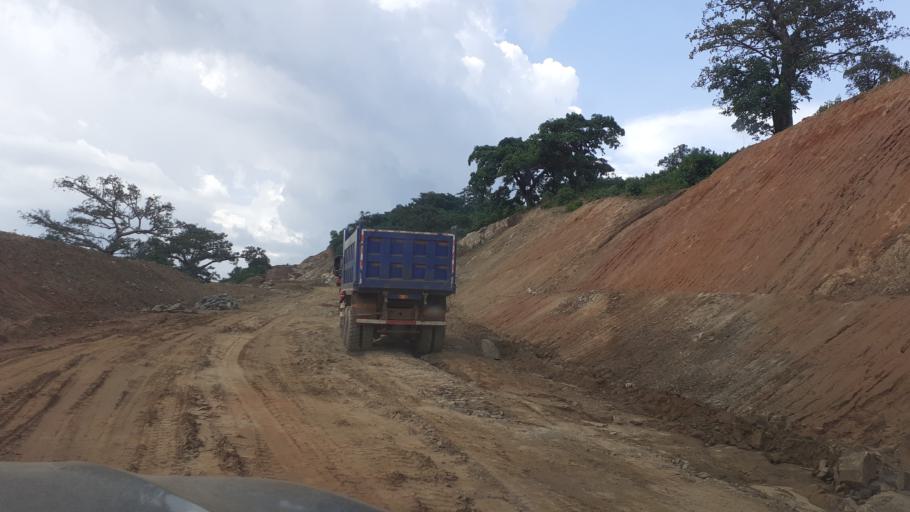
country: ET
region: Oromiya
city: Gimbi
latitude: 9.3230
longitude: 35.6920
